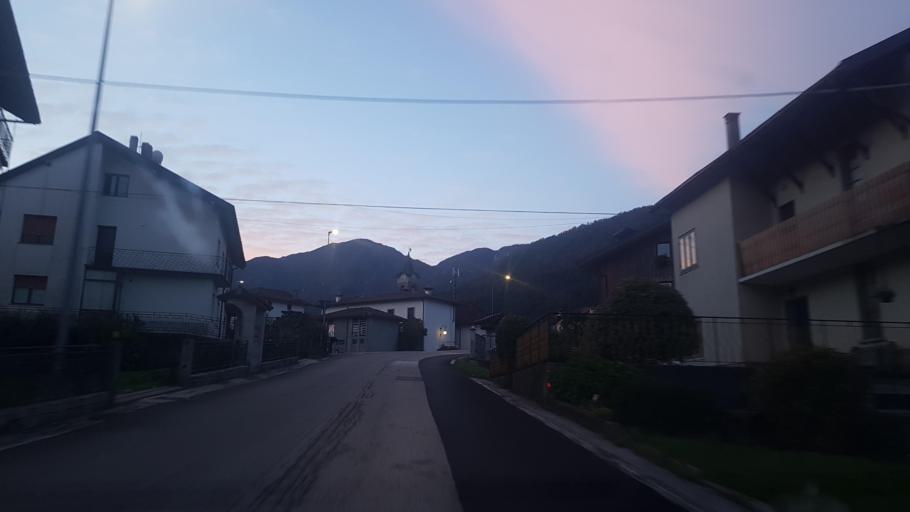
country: IT
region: Friuli Venezia Giulia
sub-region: Provincia di Udine
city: Chiaulis
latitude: 46.3845
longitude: 12.9921
